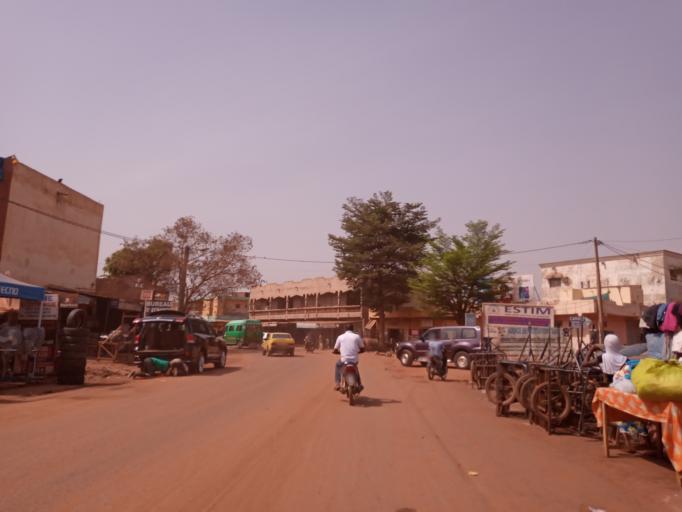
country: ML
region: Bamako
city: Bamako
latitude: 12.5896
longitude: -7.9659
